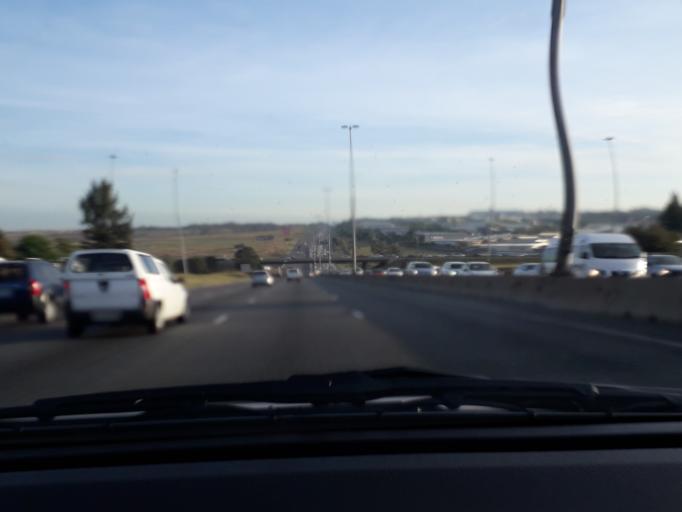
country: ZA
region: Gauteng
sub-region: City of Johannesburg Metropolitan Municipality
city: Midrand
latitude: -25.9570
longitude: 28.1333
